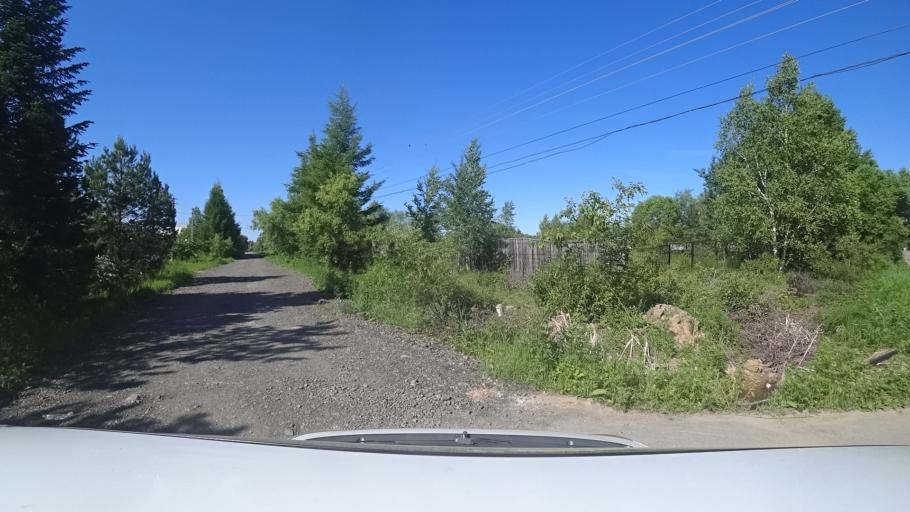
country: RU
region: Khabarovsk Krai
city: Topolevo
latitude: 48.5503
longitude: 135.1708
